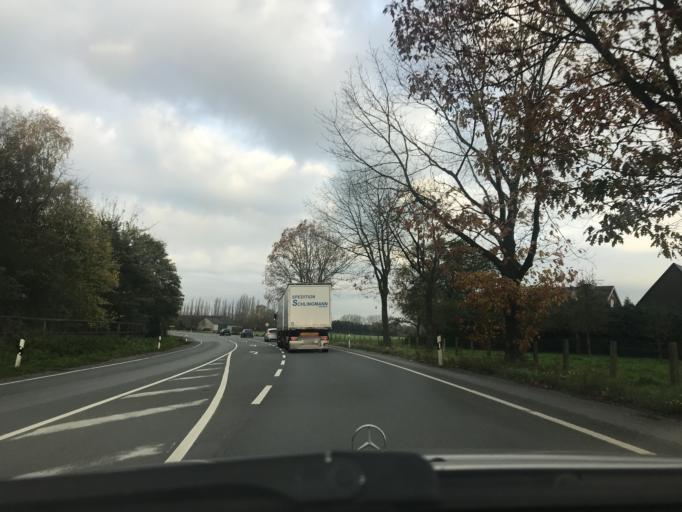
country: DE
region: North Rhine-Westphalia
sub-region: Regierungsbezirk Arnsberg
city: Welver
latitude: 51.6876
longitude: 7.9924
